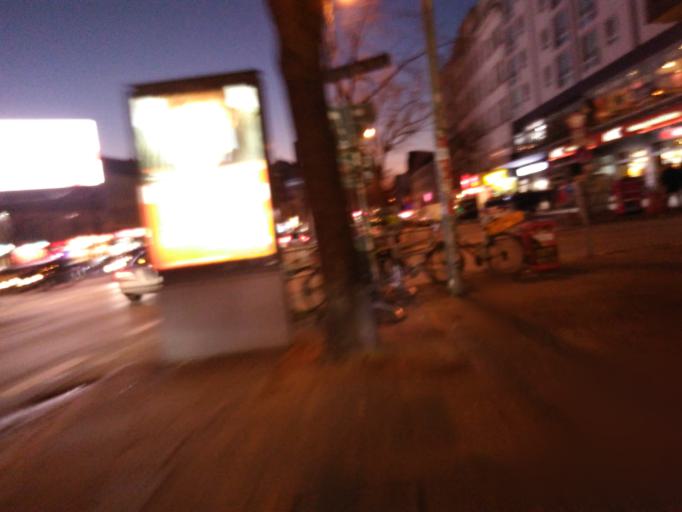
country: DE
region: Hamburg
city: St. Pauli
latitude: 53.5497
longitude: 9.9619
